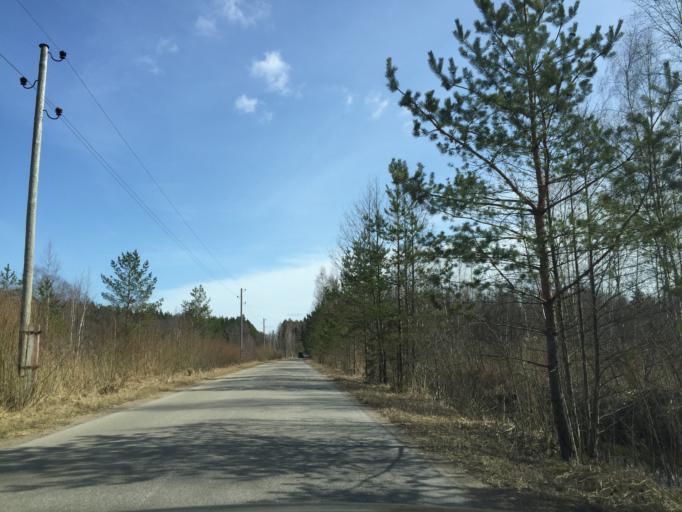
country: LV
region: Salaspils
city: Salaspils
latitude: 56.9211
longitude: 24.4179
